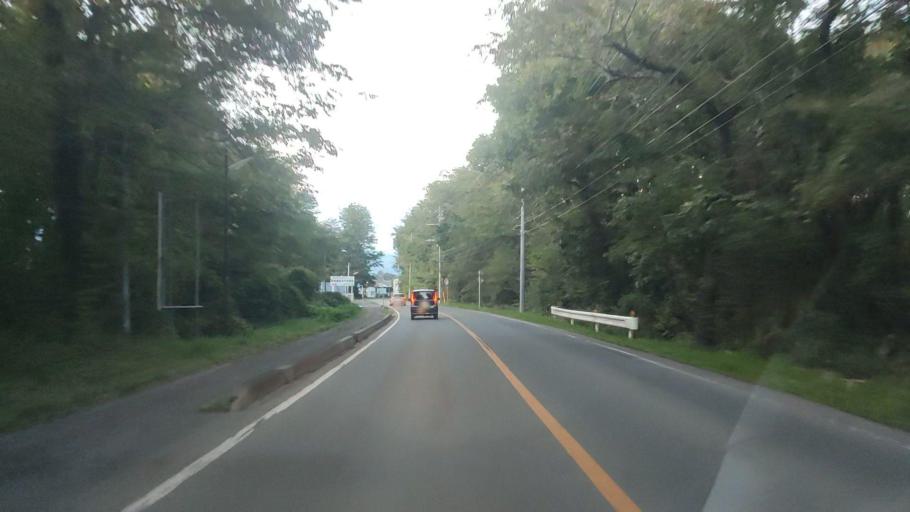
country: JP
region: Nagano
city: Komoro
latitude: 36.4955
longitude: 138.5849
